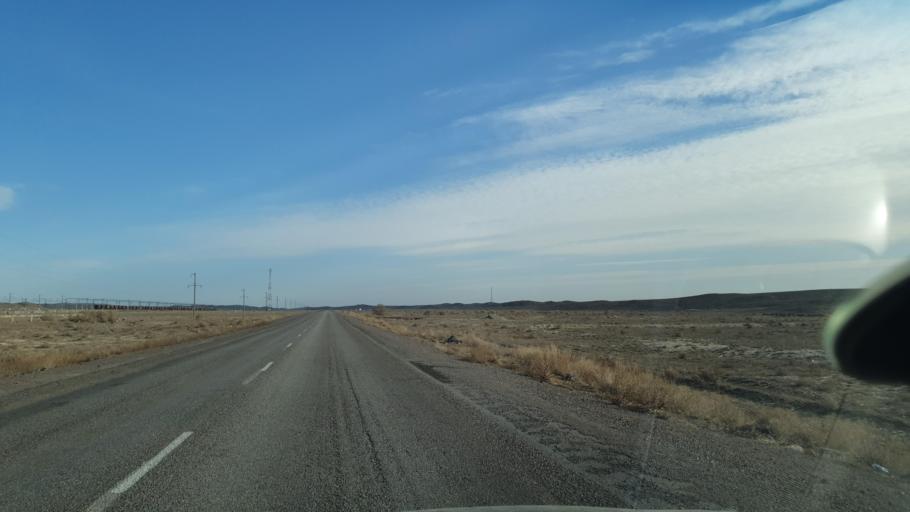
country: KZ
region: Zhambyl
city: Mynaral
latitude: 45.5585
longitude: 73.4410
